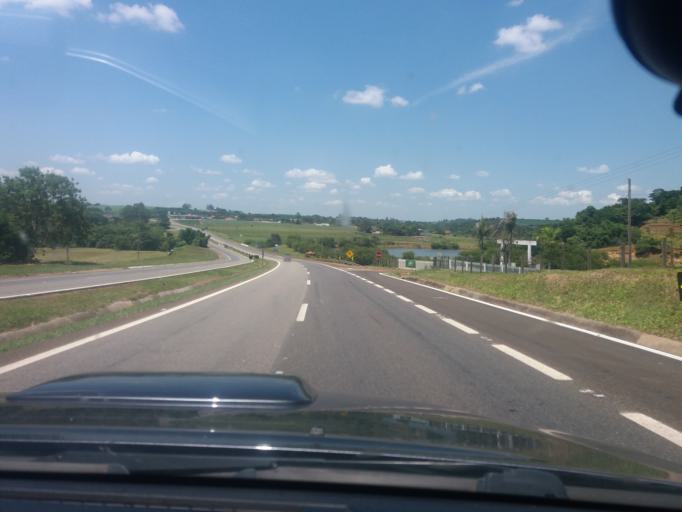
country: BR
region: Sao Paulo
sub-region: Tatui
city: Tatui
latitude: -23.3707
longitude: -47.9157
